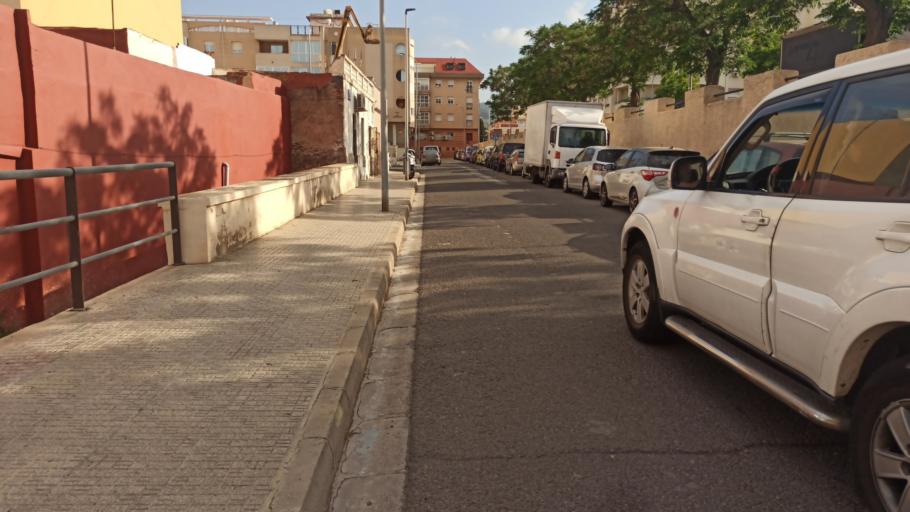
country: ES
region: Melilla
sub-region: Melilla
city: Melilla
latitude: 35.2835
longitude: -2.9491
